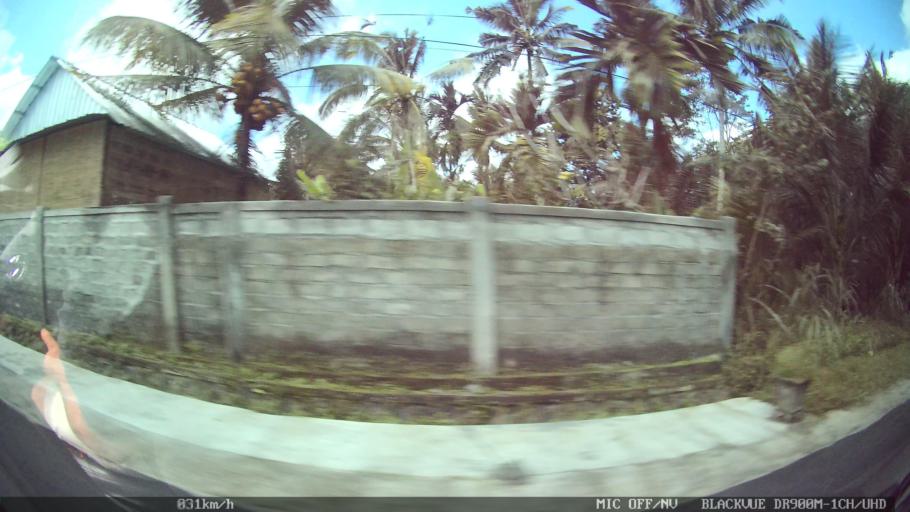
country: ID
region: Bali
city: Banjar Bebalang
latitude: -8.4765
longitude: 115.3419
